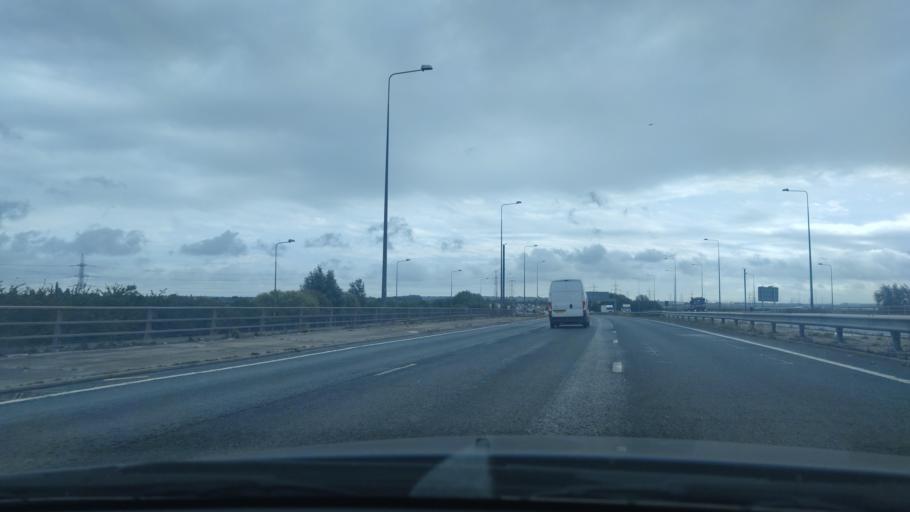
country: GB
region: England
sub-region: Greater London
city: Erith
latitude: 51.5116
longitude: 0.1862
